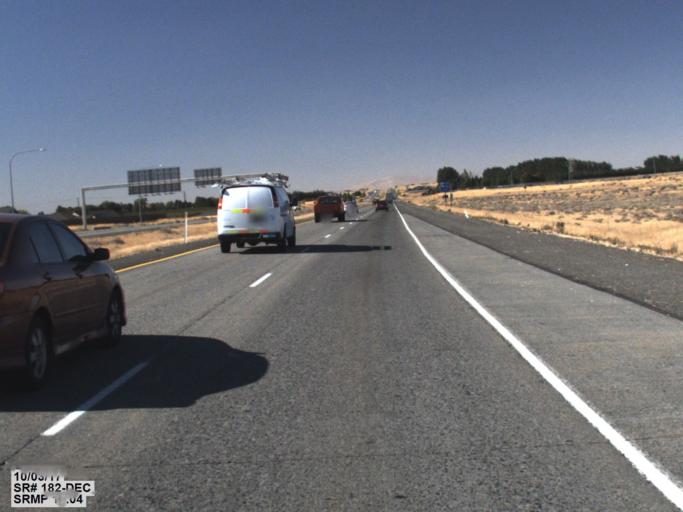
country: US
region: Washington
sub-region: Franklin County
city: Pasco
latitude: 46.2498
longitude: -119.1307
